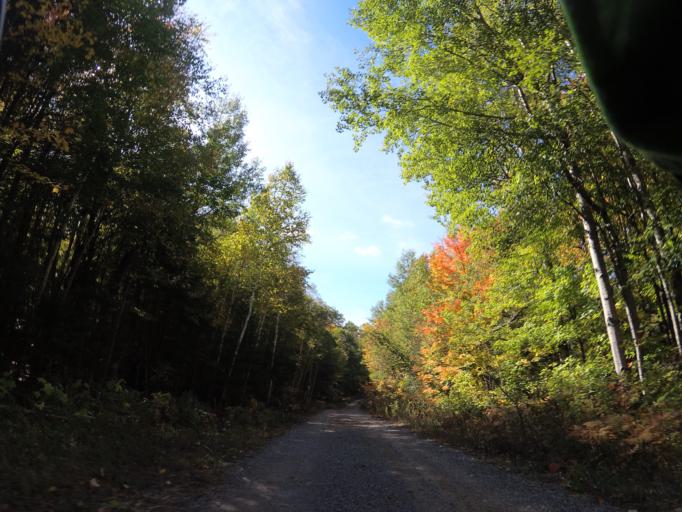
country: CA
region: Ontario
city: Renfrew
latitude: 45.3507
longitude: -77.1168
